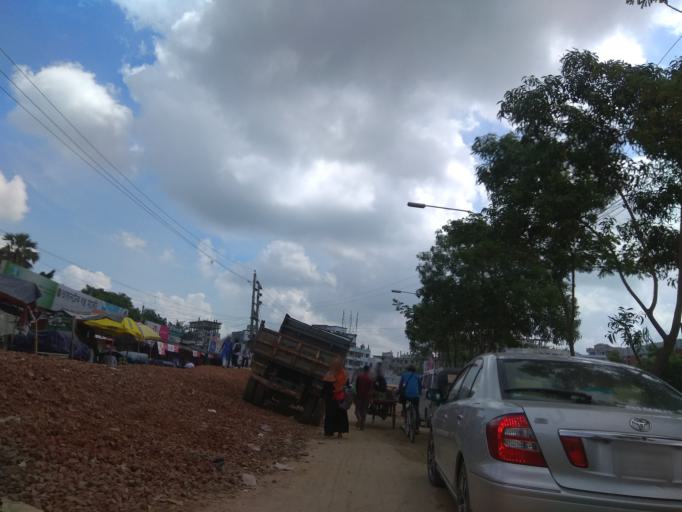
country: BD
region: Dhaka
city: Paltan
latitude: 23.8114
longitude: 90.3926
